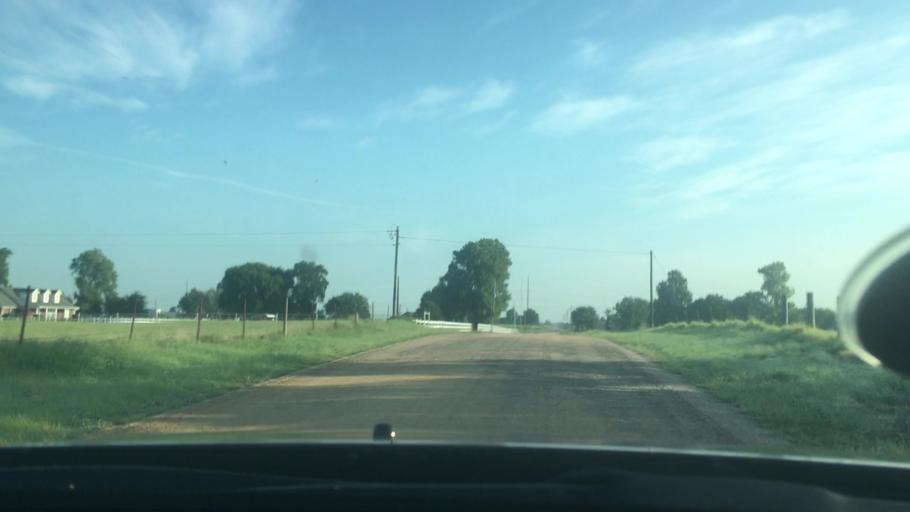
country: US
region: Oklahoma
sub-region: Pontotoc County
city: Ada
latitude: 34.8215
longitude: -96.7748
